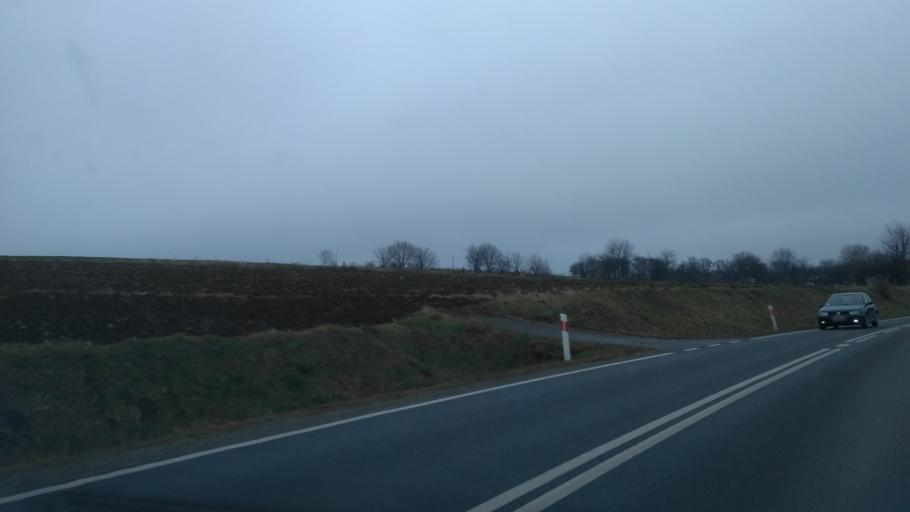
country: PL
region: Subcarpathian Voivodeship
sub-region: Powiat jaroslawski
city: Pruchnik
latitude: 49.9122
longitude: 22.5587
